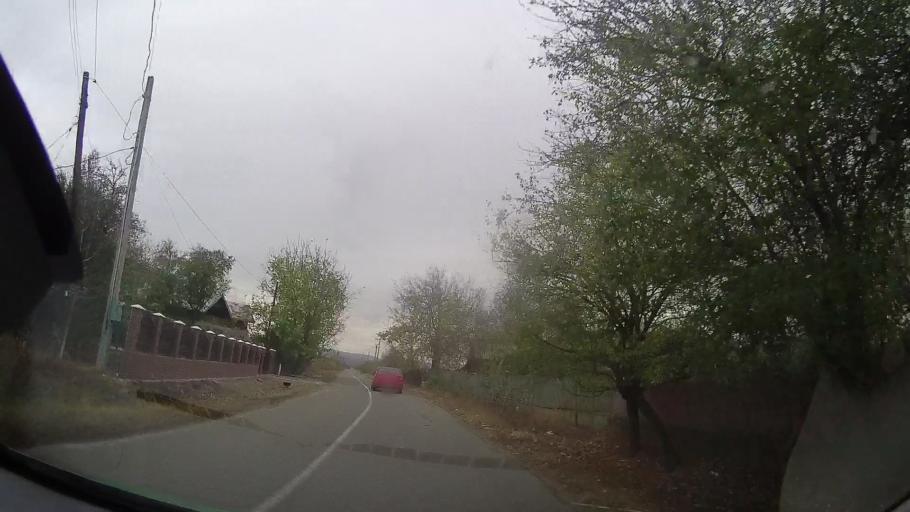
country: RO
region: Prahova
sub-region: Comuna Fantanele
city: Fantanele
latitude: 45.0157
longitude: 26.3802
